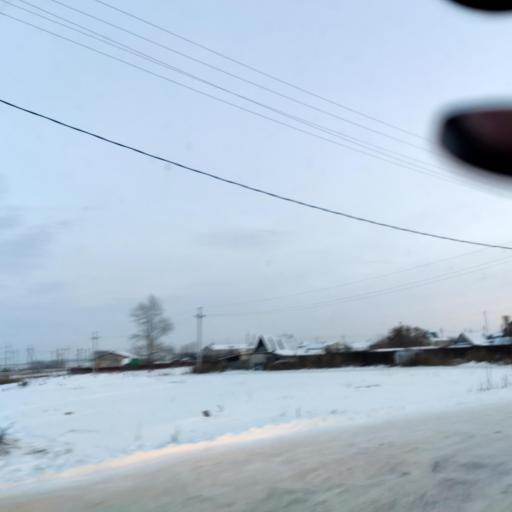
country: RU
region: Bashkortostan
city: Mikhaylovka
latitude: 54.8699
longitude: 55.7349
